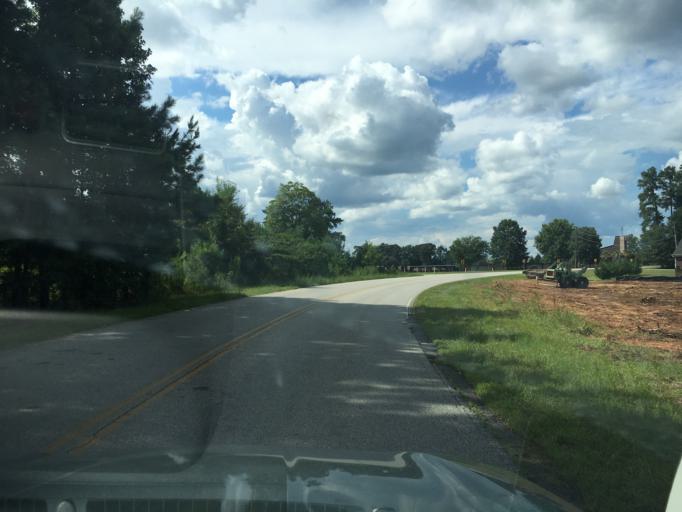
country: US
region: South Carolina
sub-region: Spartanburg County
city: Southern Shops
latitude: 35.0016
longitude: -81.9907
